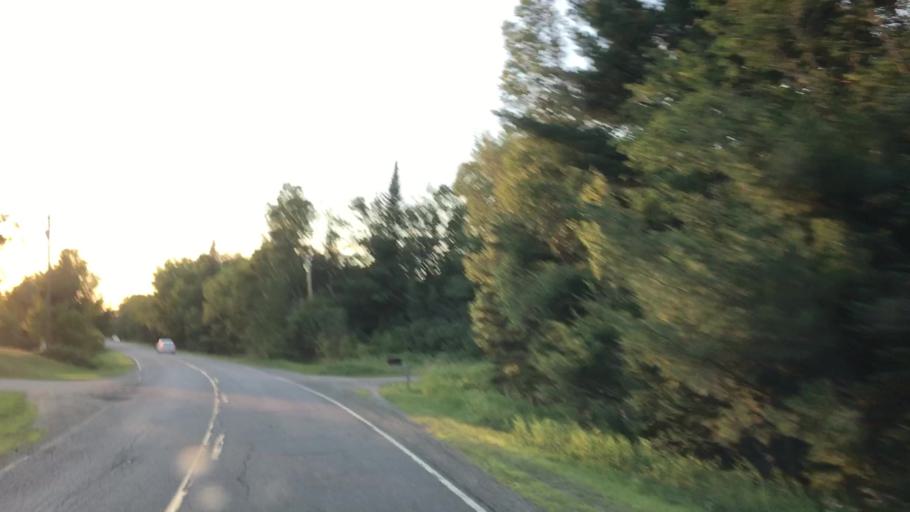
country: US
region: Maine
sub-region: Penobscot County
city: Medway
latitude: 45.5946
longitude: -68.2399
